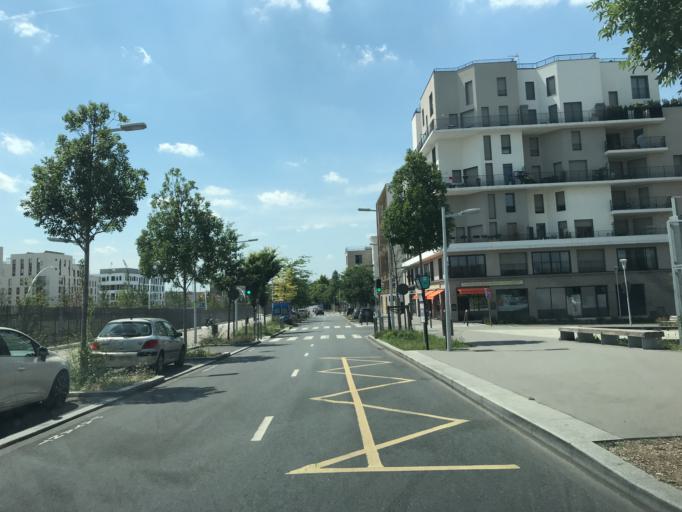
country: FR
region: Ile-de-France
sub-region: Departement des Hauts-de-Seine
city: Nanterre
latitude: 48.9000
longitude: 2.1999
